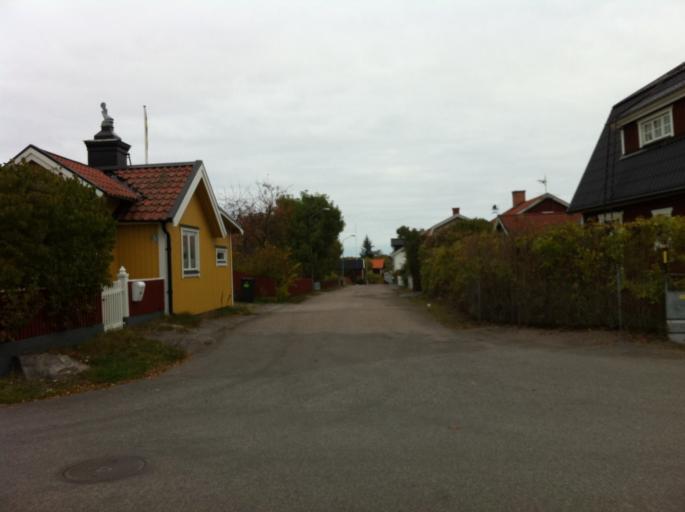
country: SE
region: Uppsala
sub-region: Osthammars Kommun
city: Oregrund
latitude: 60.3375
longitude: 18.4455
